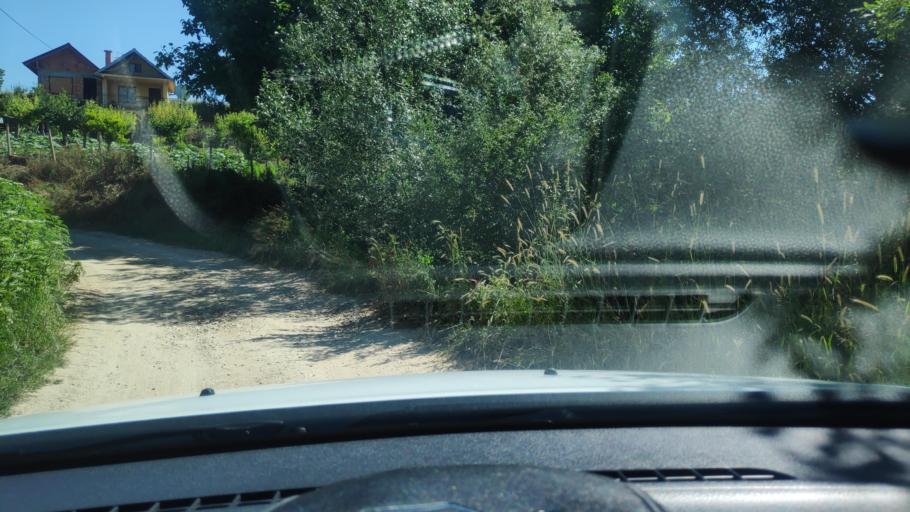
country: MK
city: Klechovce
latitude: 42.0655
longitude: 21.8575
